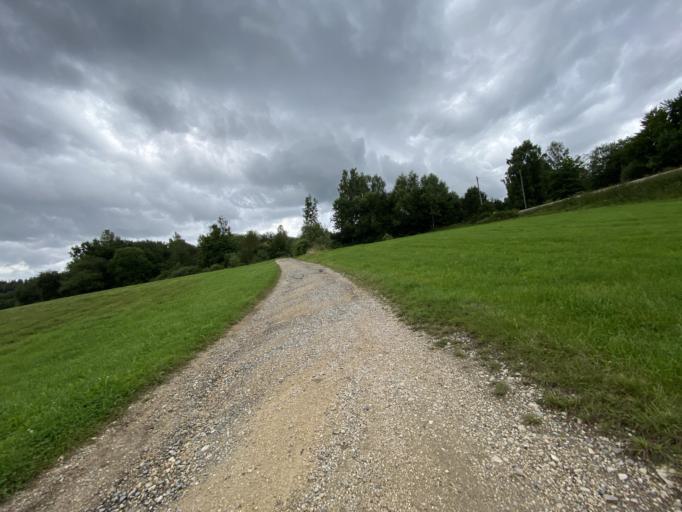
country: DE
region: Baden-Wuerttemberg
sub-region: Tuebingen Region
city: Sigmaringen
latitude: 48.1021
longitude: 9.2341
